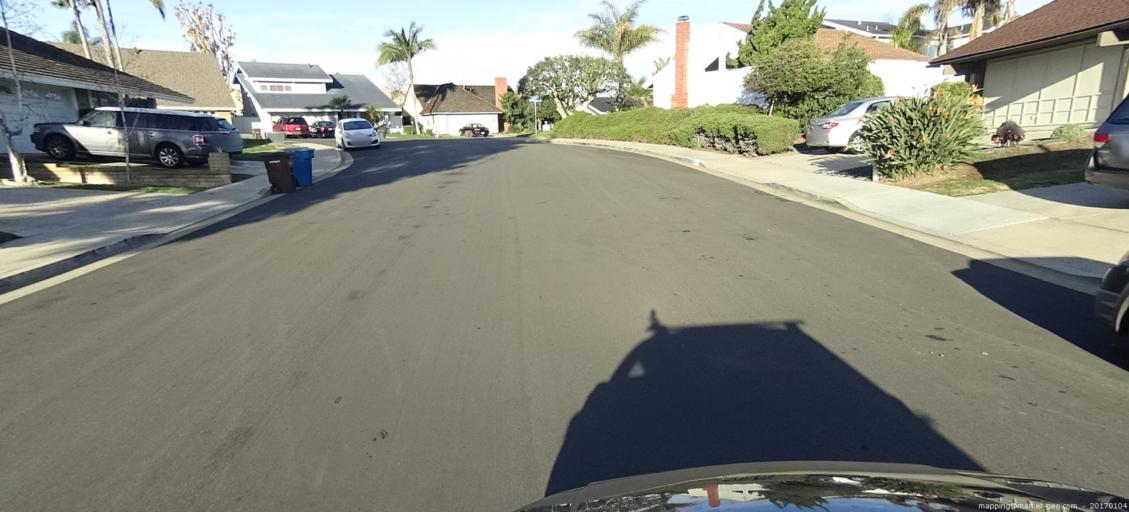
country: US
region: California
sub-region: Orange County
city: Dana Point
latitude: 33.4833
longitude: -117.7055
